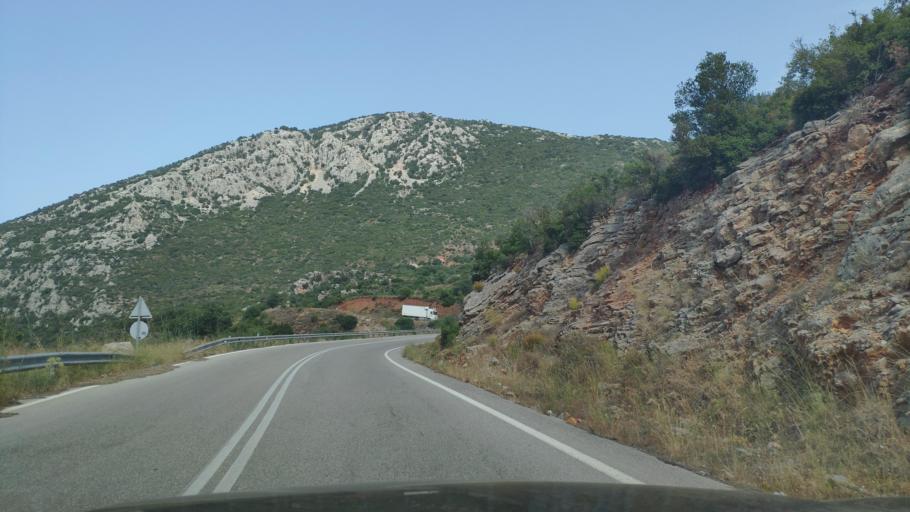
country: GR
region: Peloponnese
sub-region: Nomos Argolidos
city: Palaia Epidavros
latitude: 37.6024
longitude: 23.1610
